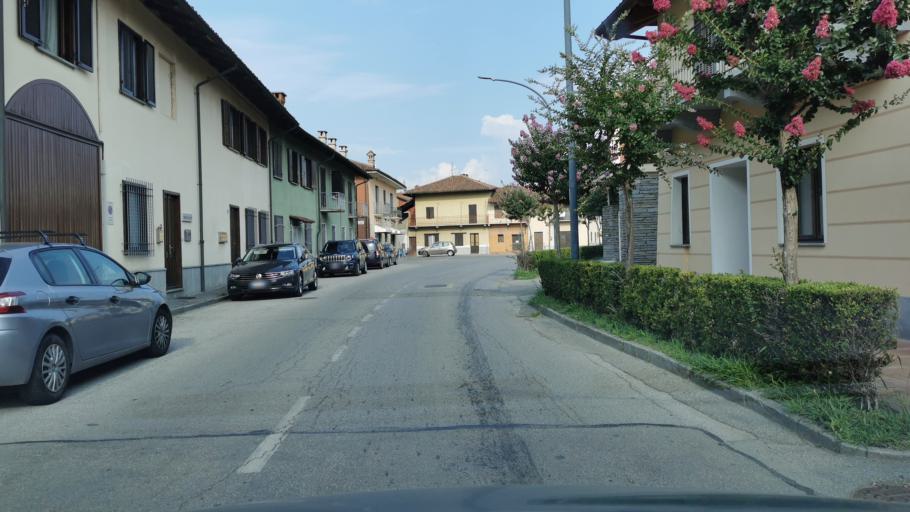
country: IT
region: Piedmont
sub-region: Provincia di Torino
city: Vigone
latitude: 44.8424
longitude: 7.4979
